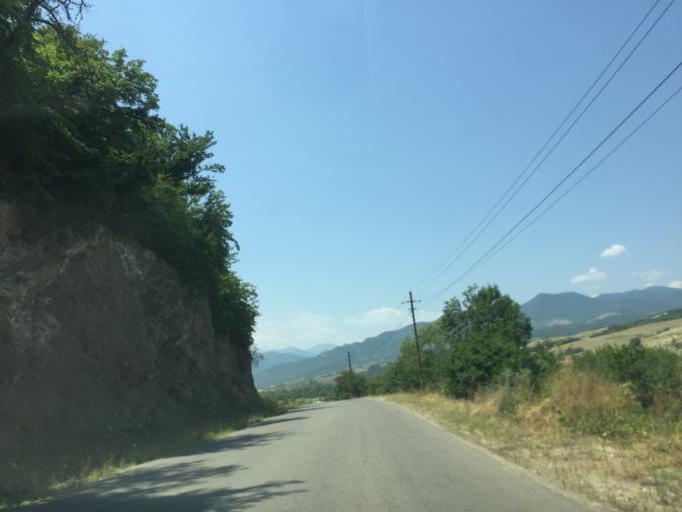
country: AZ
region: Tartar Rayon
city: Martakert
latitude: 40.1356
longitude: 46.4872
